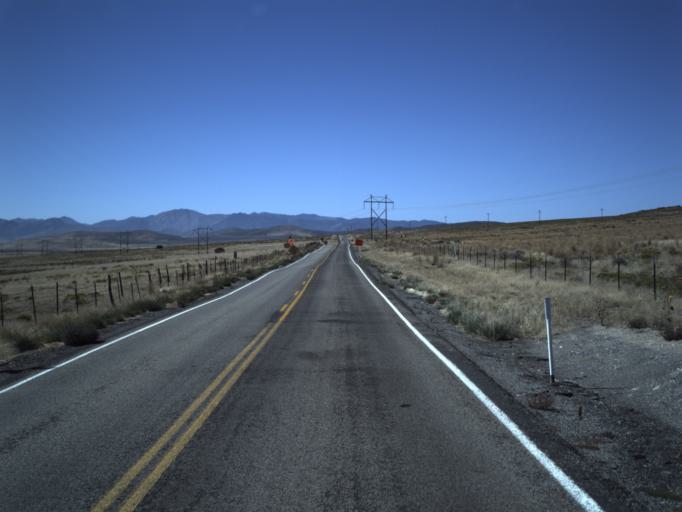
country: US
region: Utah
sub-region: Utah County
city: Eagle Mountain
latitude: 40.1830
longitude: -111.9128
